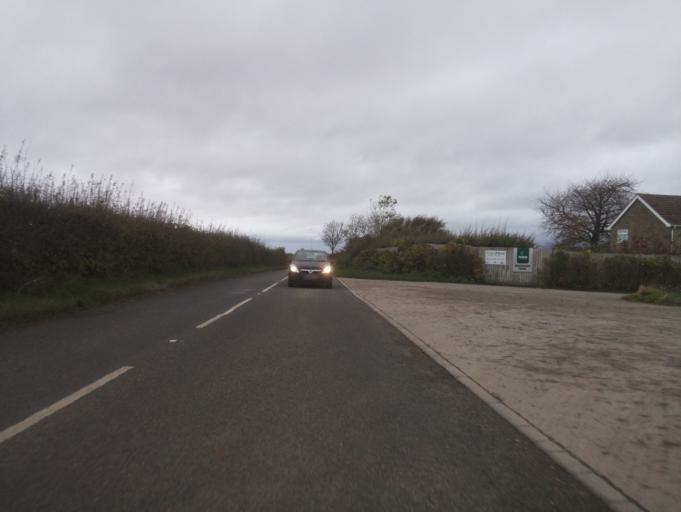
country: GB
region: England
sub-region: Dorset
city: Sherborne
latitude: 50.9722
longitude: -2.5561
